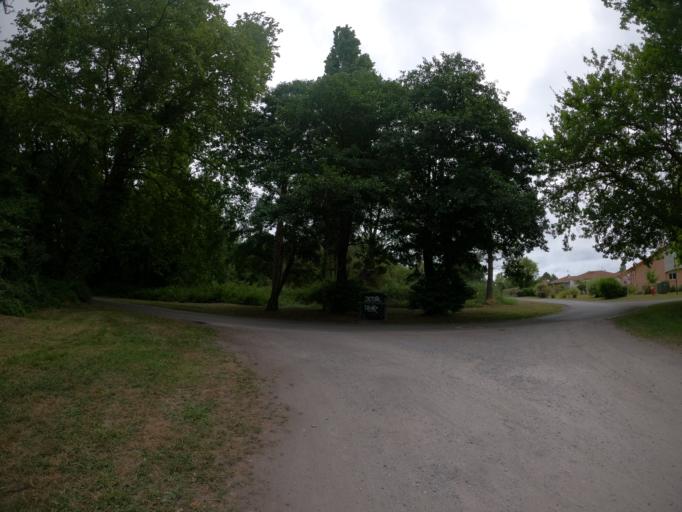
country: FR
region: Aquitaine
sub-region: Departement des Landes
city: Leon
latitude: 43.8851
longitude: -1.3077
